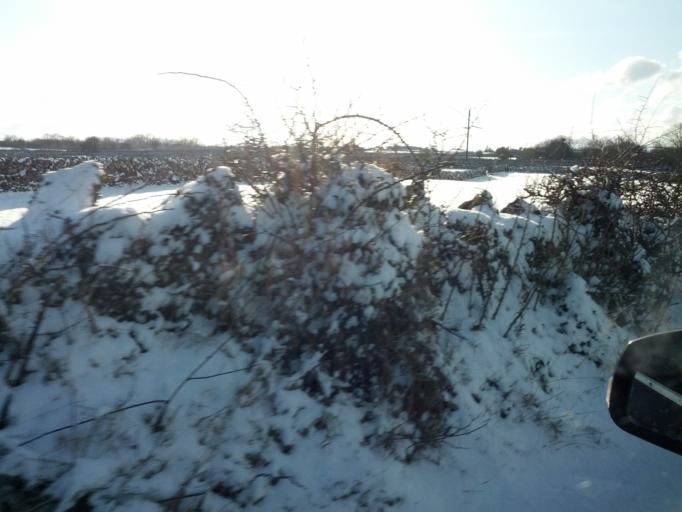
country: IE
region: Connaught
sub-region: County Galway
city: Oranmore
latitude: 53.2005
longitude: -8.8459
